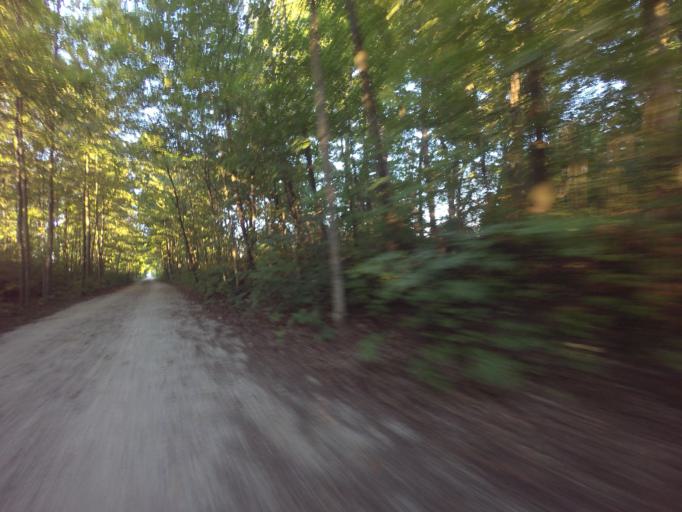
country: CA
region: Ontario
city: Brampton
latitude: 43.8847
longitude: -79.8450
